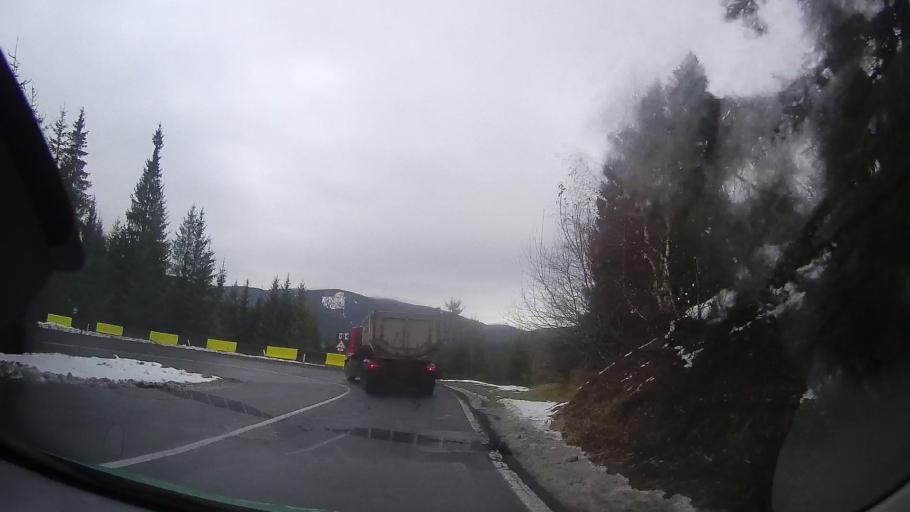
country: RO
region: Harghita
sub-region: Municipiul Gheorgheni
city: Gheorgheni
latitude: 46.7748
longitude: 25.6986
